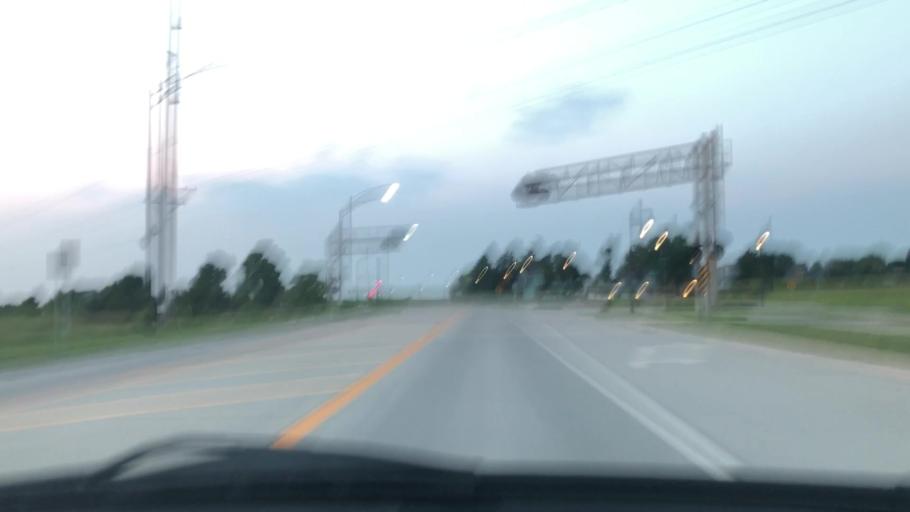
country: US
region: Iowa
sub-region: Johnson County
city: North Liberty
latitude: 41.7574
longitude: -91.6076
